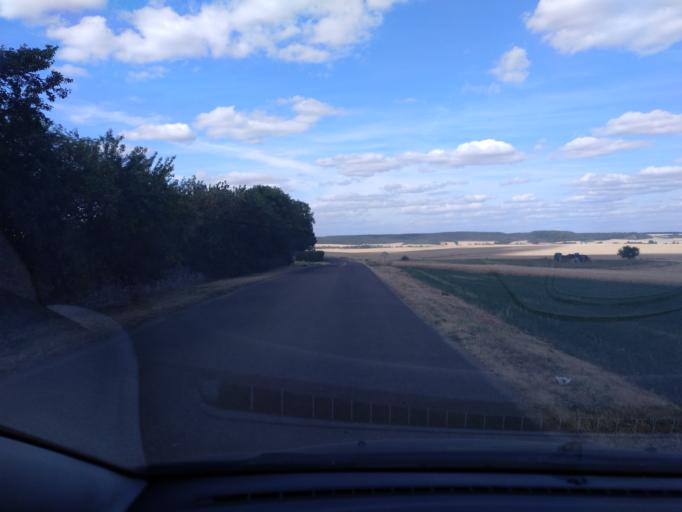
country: FR
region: Bourgogne
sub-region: Departement de la Cote-d'Or
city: Chatillon-sur-Seine
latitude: 47.9193
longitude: 4.6316
